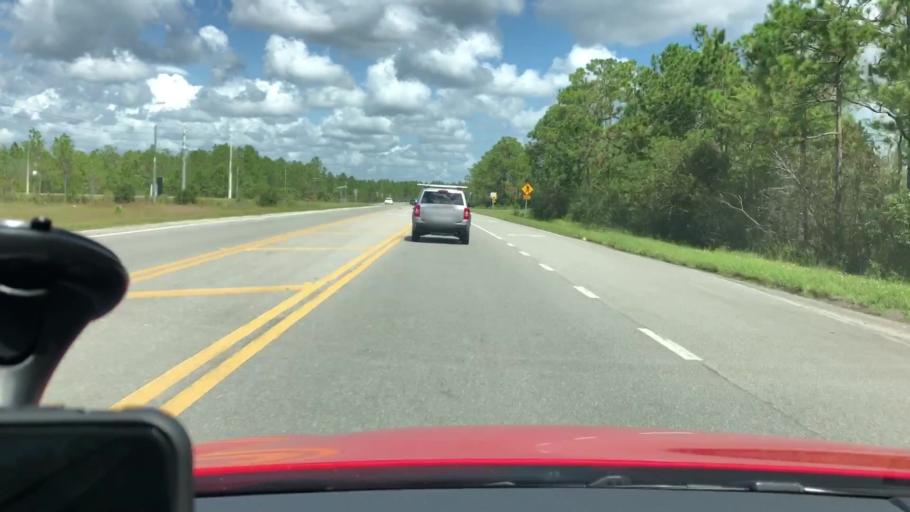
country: US
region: Florida
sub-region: Volusia County
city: Holly Hill
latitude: 29.2066
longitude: -81.1198
